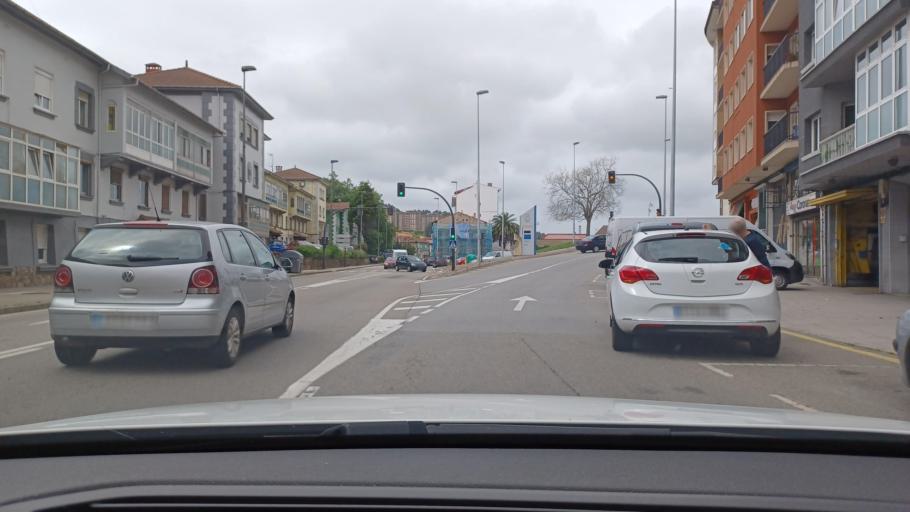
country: ES
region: Asturias
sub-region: Province of Asturias
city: Aviles
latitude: 43.5641
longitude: -5.9257
